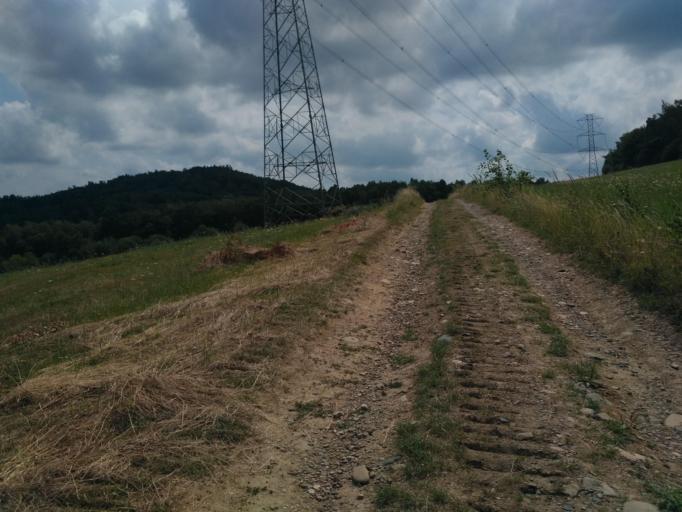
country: PL
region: Subcarpathian Voivodeship
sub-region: Powiat krosnienski
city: Iwonicz-Zdroj
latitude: 49.5896
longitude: 21.7761
